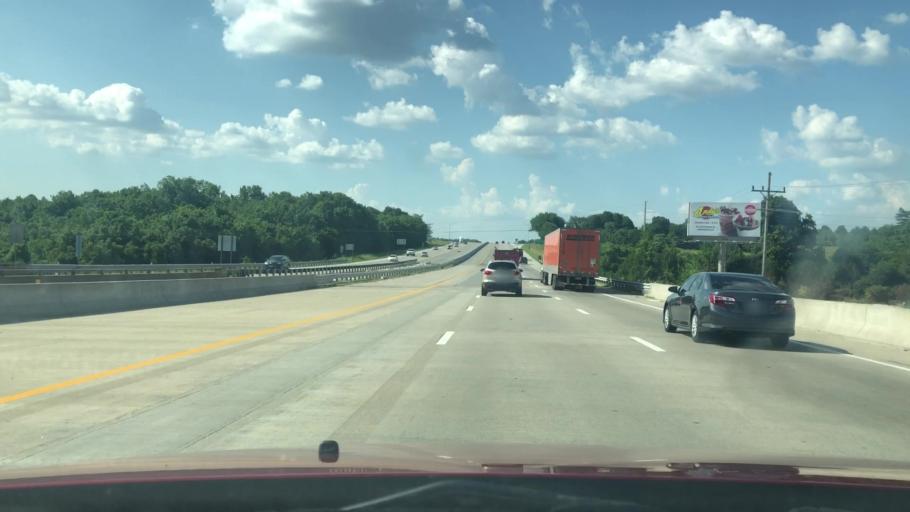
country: US
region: Missouri
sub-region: Christian County
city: Ozark
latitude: 37.0910
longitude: -93.2311
